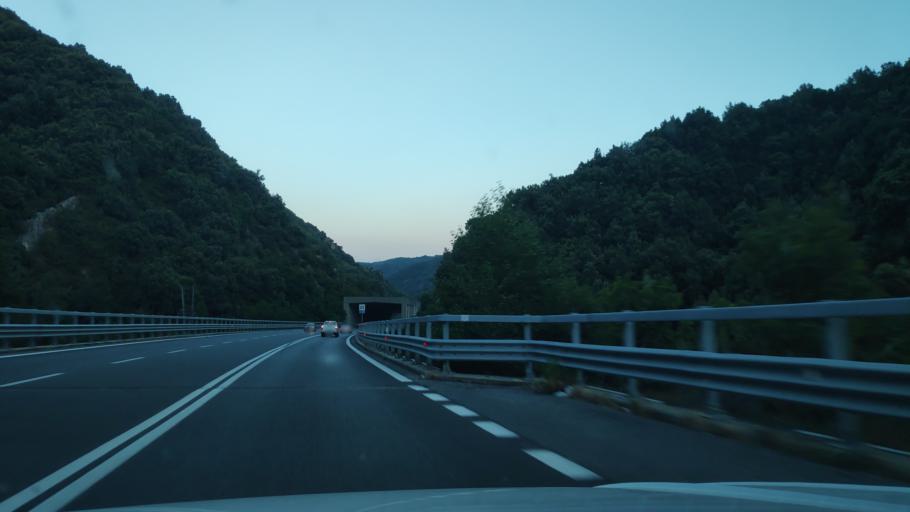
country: IT
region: Calabria
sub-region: Provincia di Reggio Calabria
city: Amato
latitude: 38.3722
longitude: 16.1801
